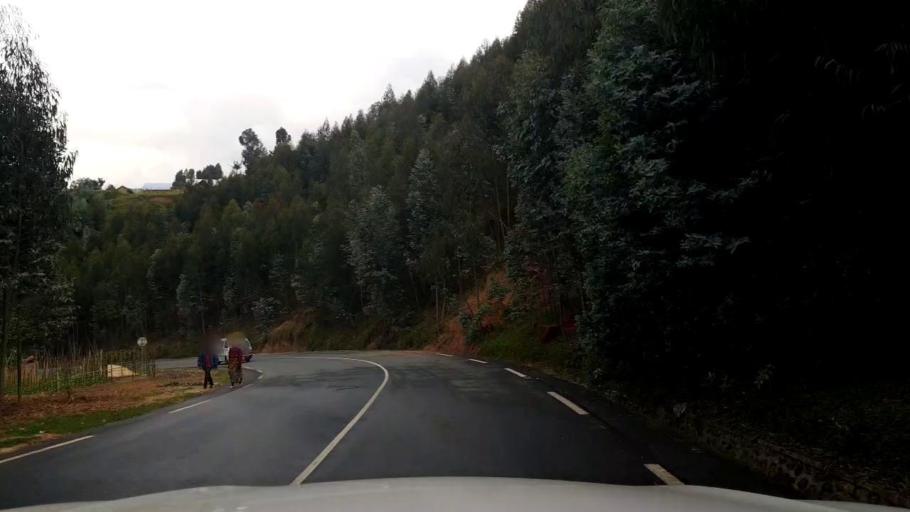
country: RW
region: Northern Province
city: Musanze
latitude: -1.6868
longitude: 29.5209
